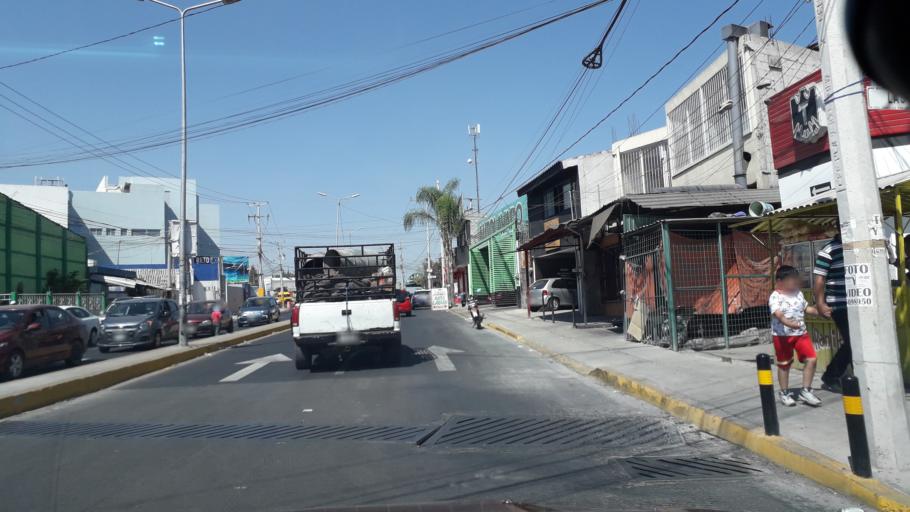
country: MX
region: Puebla
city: Puebla
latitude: 18.9942
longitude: -98.2126
